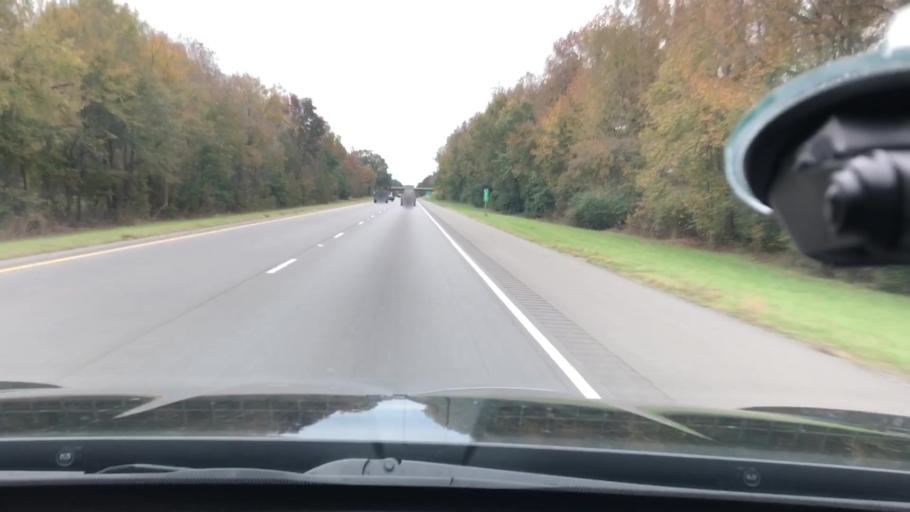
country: US
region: Arkansas
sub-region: Hempstead County
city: Hope
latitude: 33.6449
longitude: -93.6854
